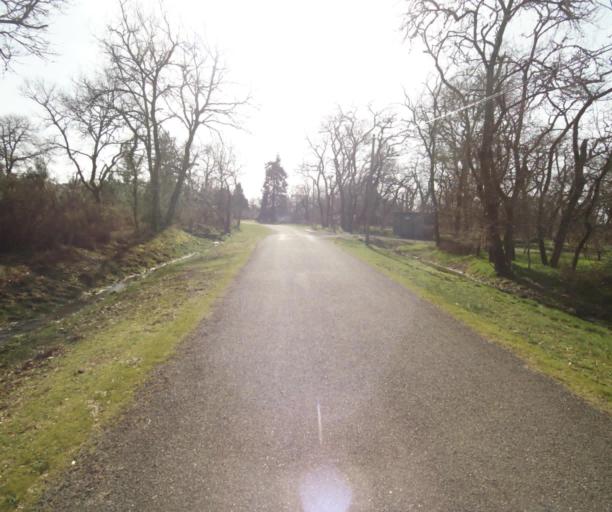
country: FR
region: Aquitaine
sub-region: Departement des Landes
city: Roquefort
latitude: 44.1285
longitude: -0.1917
